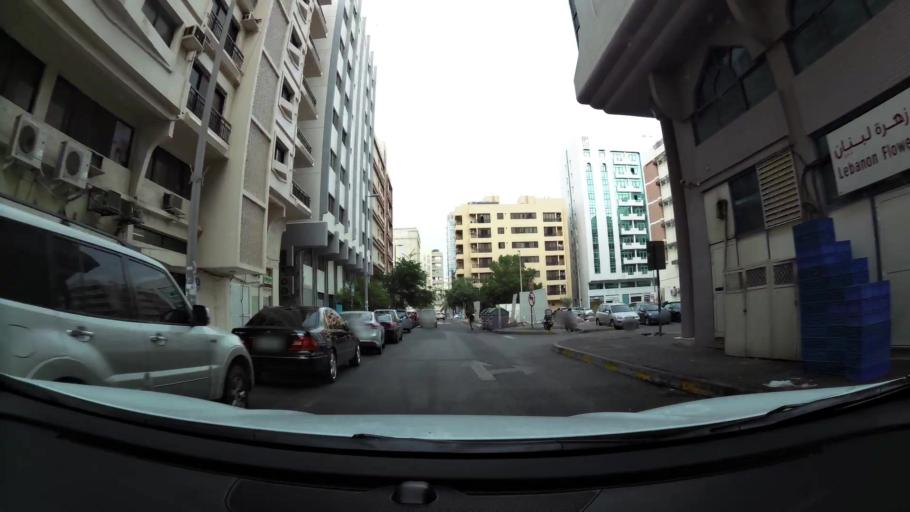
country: AE
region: Abu Dhabi
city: Abu Dhabi
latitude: 24.4895
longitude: 54.3819
